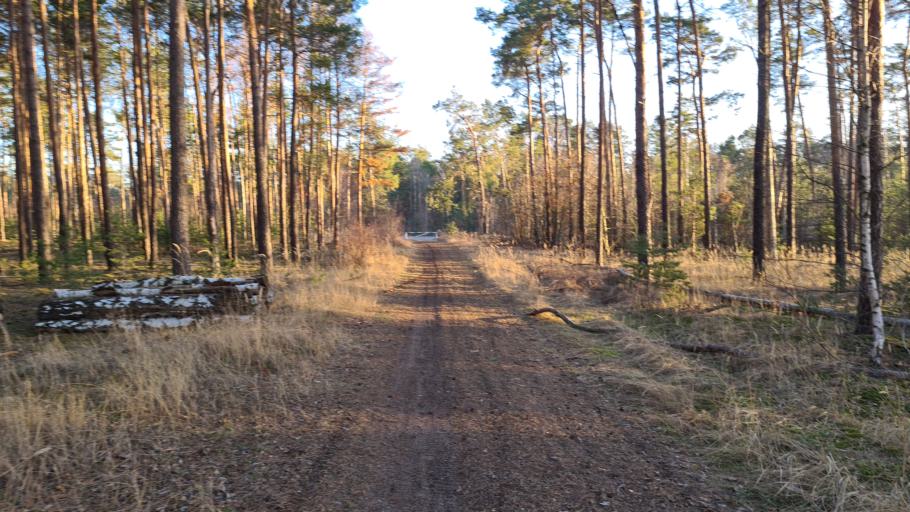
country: DE
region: Brandenburg
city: Finsterwalde
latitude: 51.6339
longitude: 13.6609
